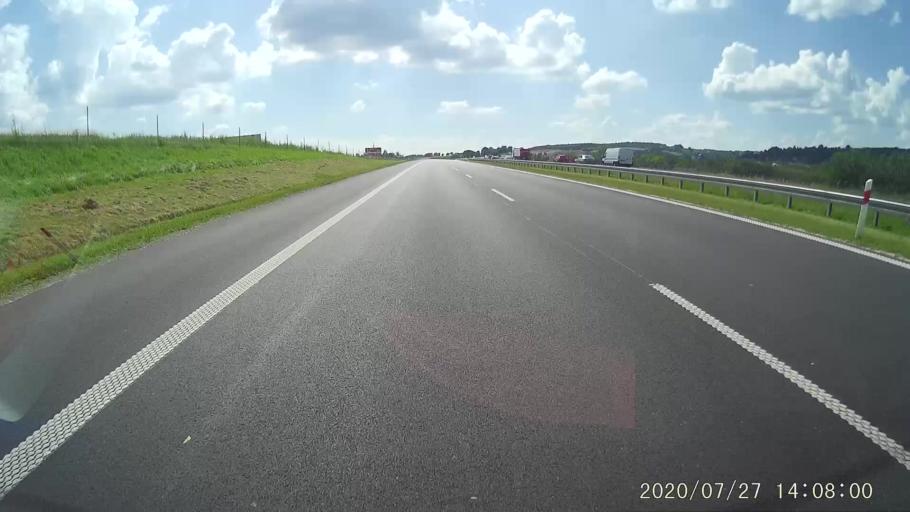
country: PL
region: Lesser Poland Voivodeship
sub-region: Powiat krakowski
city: Mnikow
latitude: 50.0770
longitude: 19.7394
